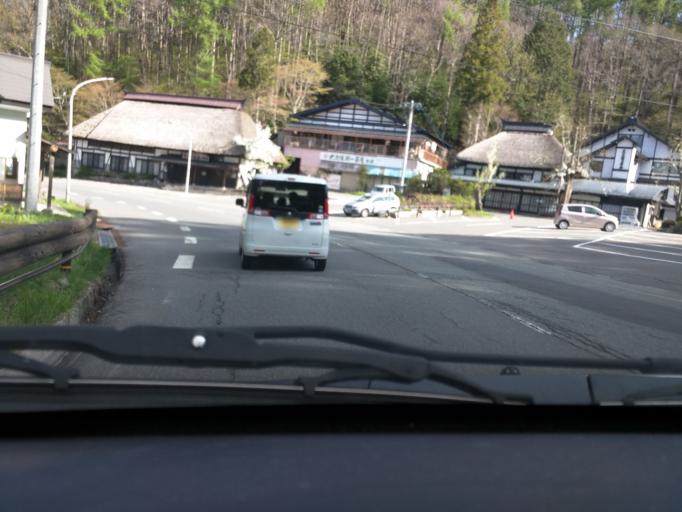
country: JP
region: Nagano
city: Nagano-shi
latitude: 36.7152
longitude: 138.1151
